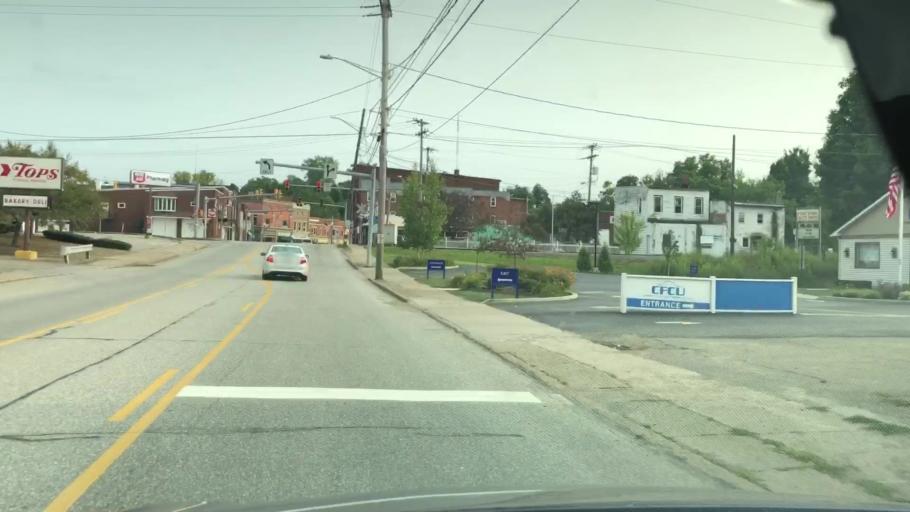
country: US
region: Pennsylvania
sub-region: Erie County
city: Union City
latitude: 41.9004
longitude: -79.8455
